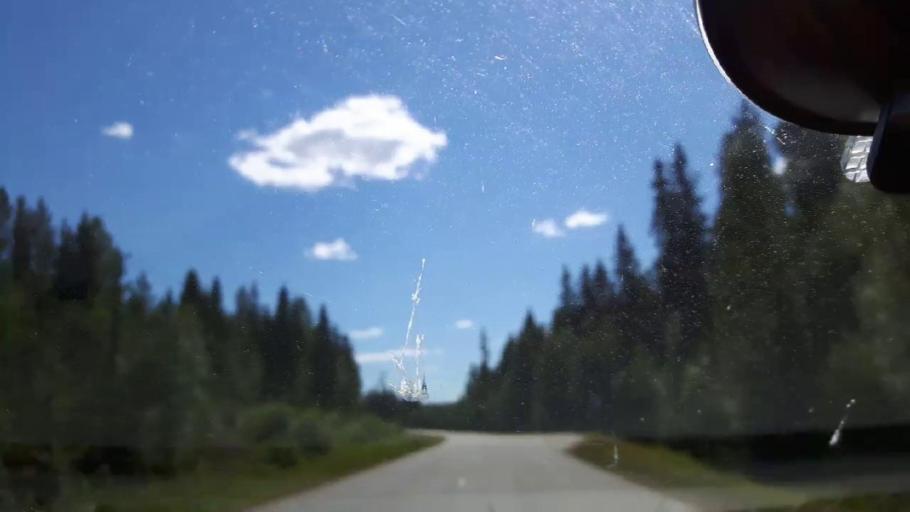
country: SE
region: Vaesternorrland
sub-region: Ange Kommun
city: Fransta
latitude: 62.7347
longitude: 16.3301
